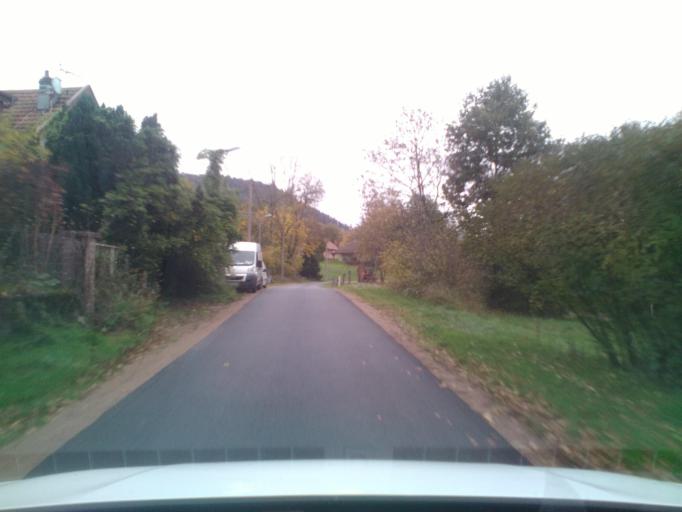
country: FR
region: Lorraine
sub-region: Departement des Vosges
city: Senones
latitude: 48.3896
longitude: 6.9541
